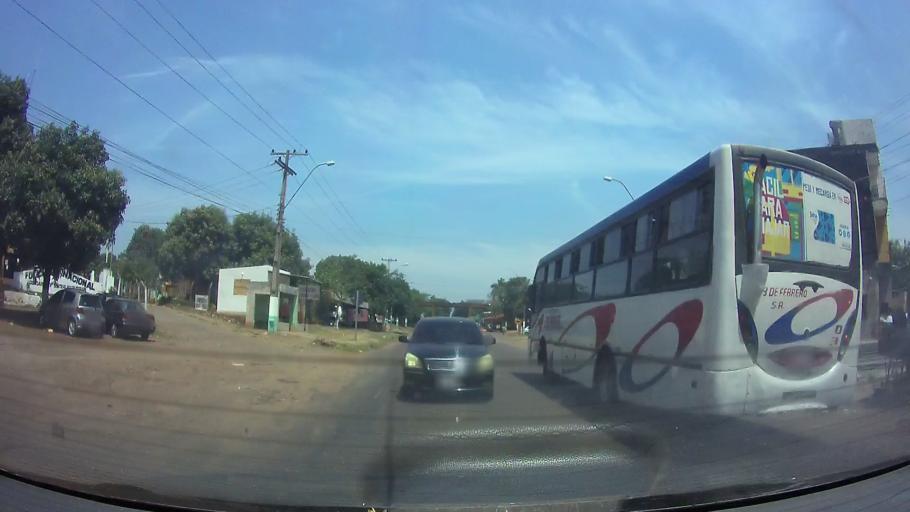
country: PY
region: Central
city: Guarambare
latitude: -25.4197
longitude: -57.4550
